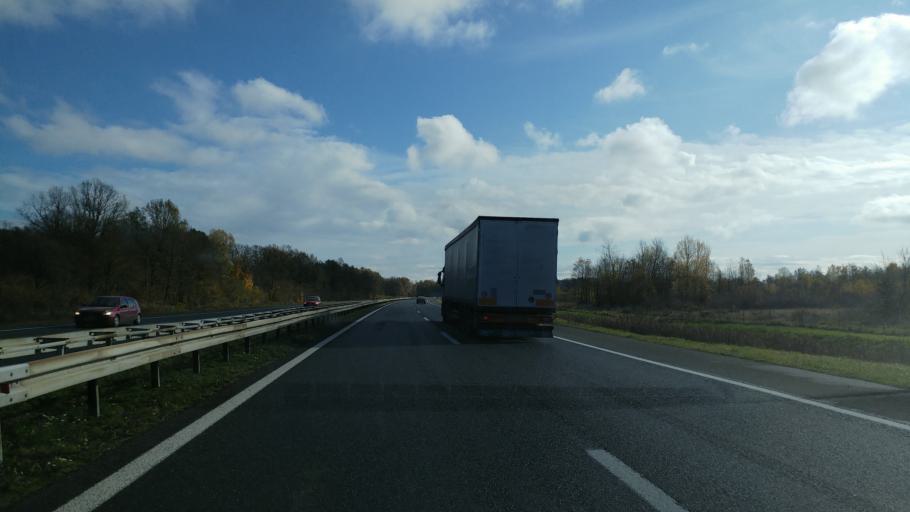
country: HR
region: Zagrebacka
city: Lupoglav
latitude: 45.7454
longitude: 16.3191
